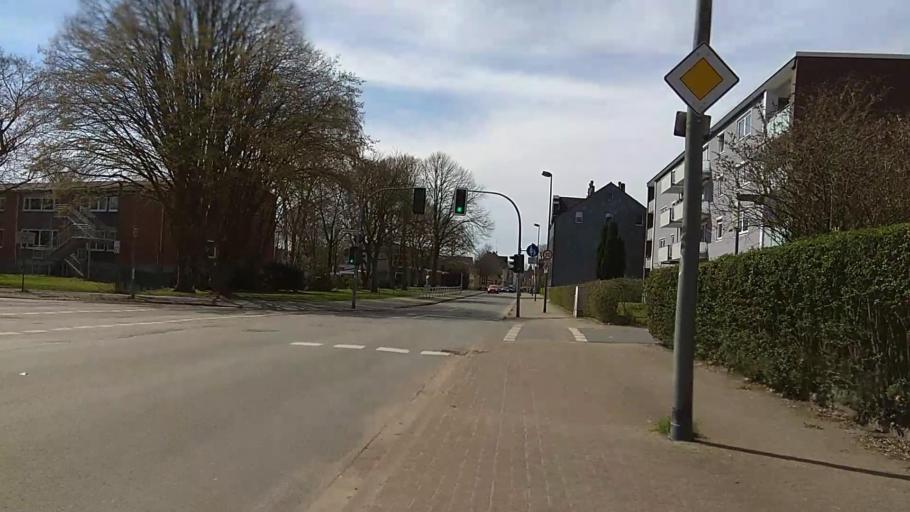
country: DE
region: North Rhine-Westphalia
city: Herten
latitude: 51.5610
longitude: 7.0962
